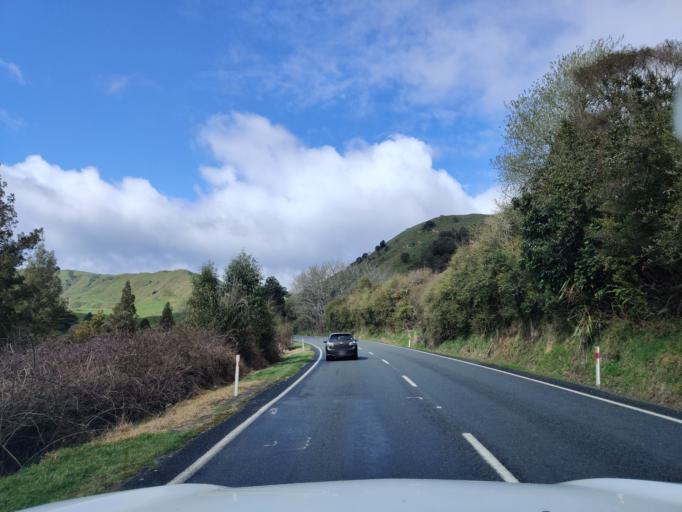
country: NZ
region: Waikato
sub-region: Otorohanga District
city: Otorohanga
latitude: -38.5902
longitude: 175.2177
